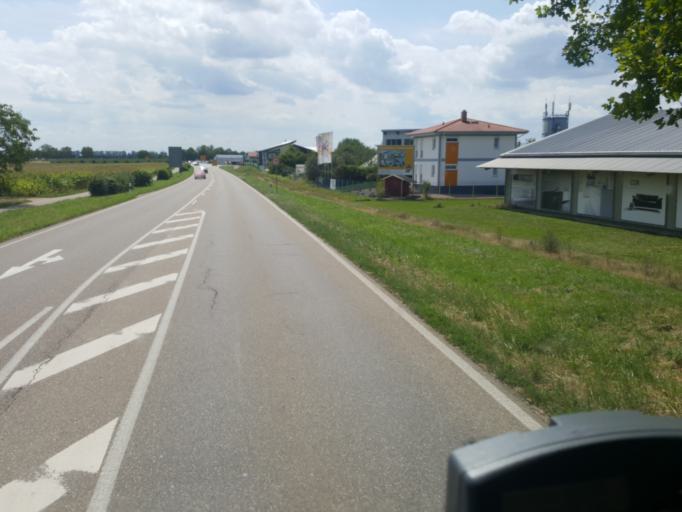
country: DE
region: Baden-Wuerttemberg
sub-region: Freiburg Region
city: Buggingen
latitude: 47.8526
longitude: 7.6310
